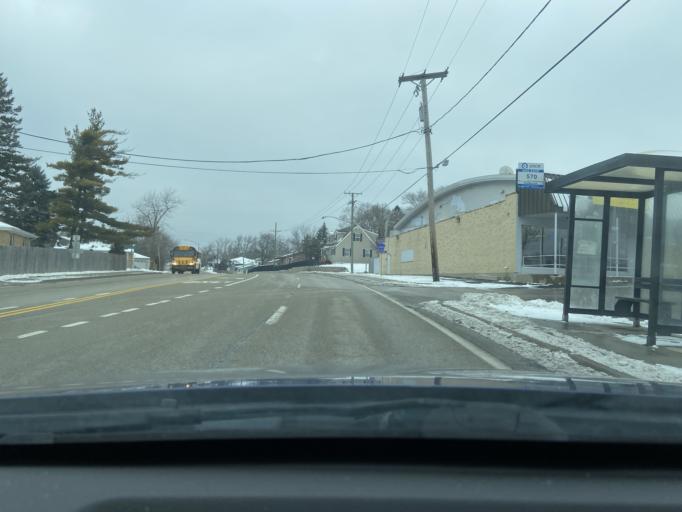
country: US
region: Illinois
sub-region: Lake County
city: Round Lake
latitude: 42.3601
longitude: -88.0900
